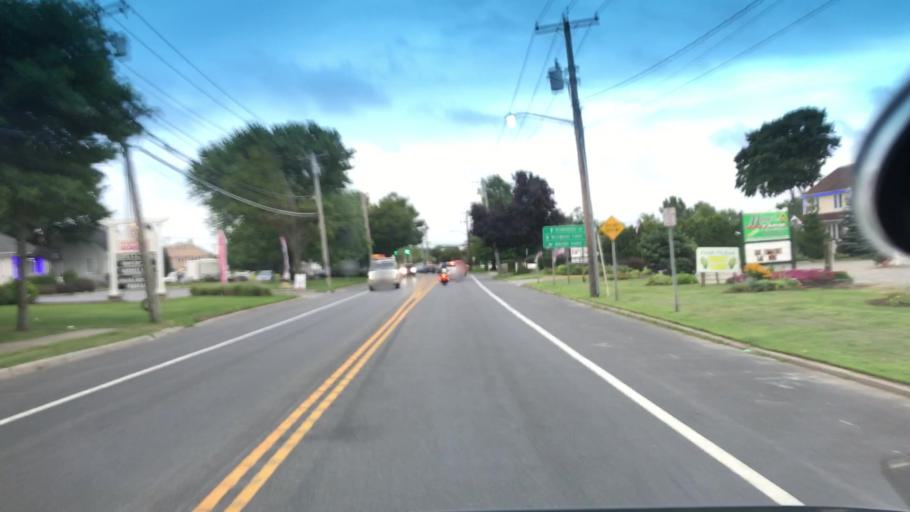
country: US
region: New York
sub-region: Suffolk County
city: Wading River
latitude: 40.9439
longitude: -72.8445
